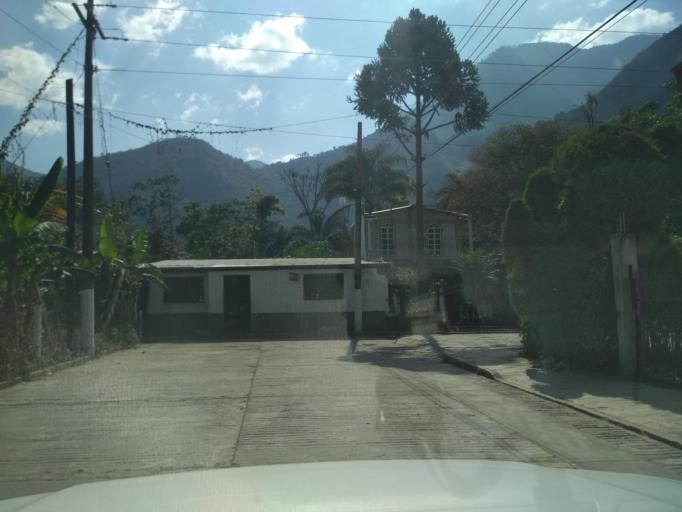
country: MX
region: Veracruz
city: Jalapilla
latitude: 18.8057
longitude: -97.1007
